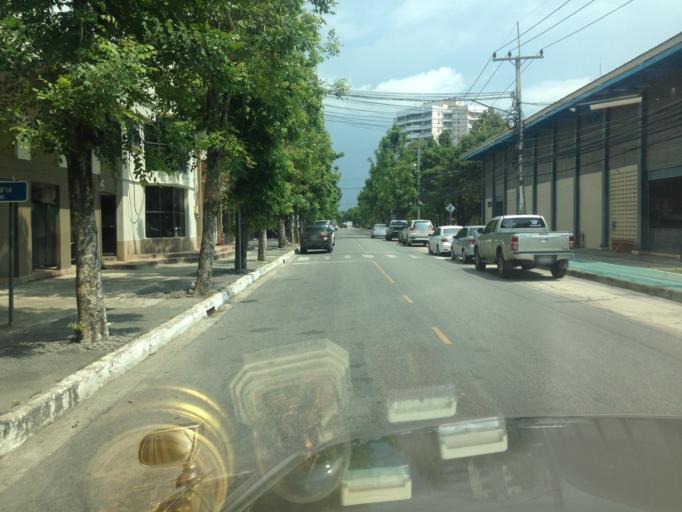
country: TH
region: Chon Buri
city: Si Racha
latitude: 13.2755
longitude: 100.9283
